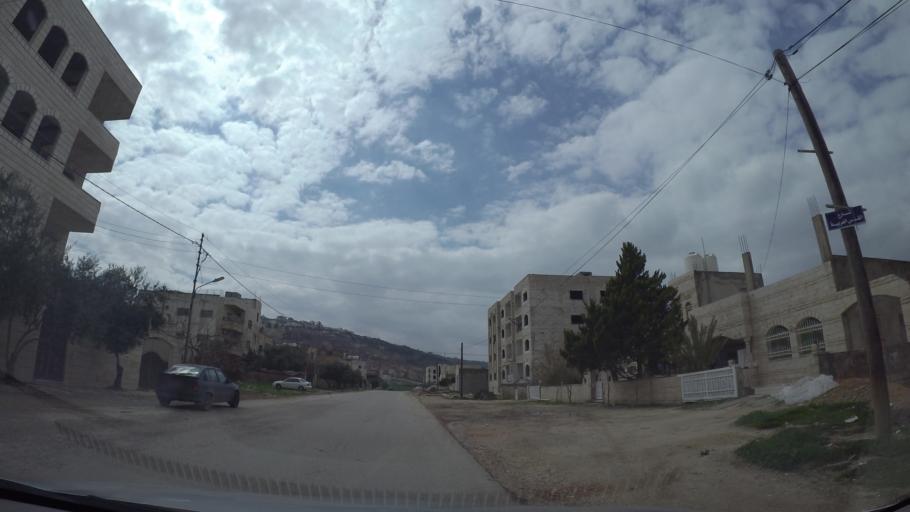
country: JO
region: Amman
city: Al Jubayhah
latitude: 32.0509
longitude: 35.8276
